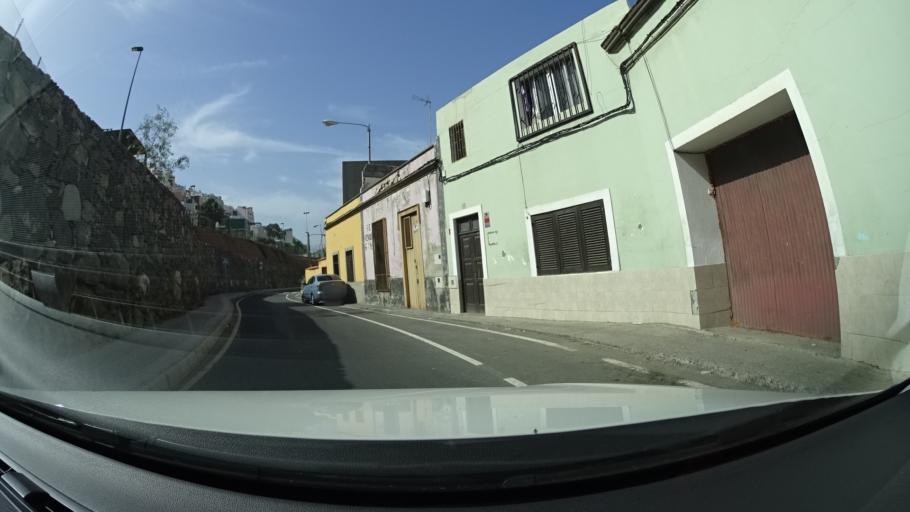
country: ES
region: Canary Islands
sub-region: Provincia de Las Palmas
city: Las Palmas de Gran Canaria
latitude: 28.0984
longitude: -15.4207
